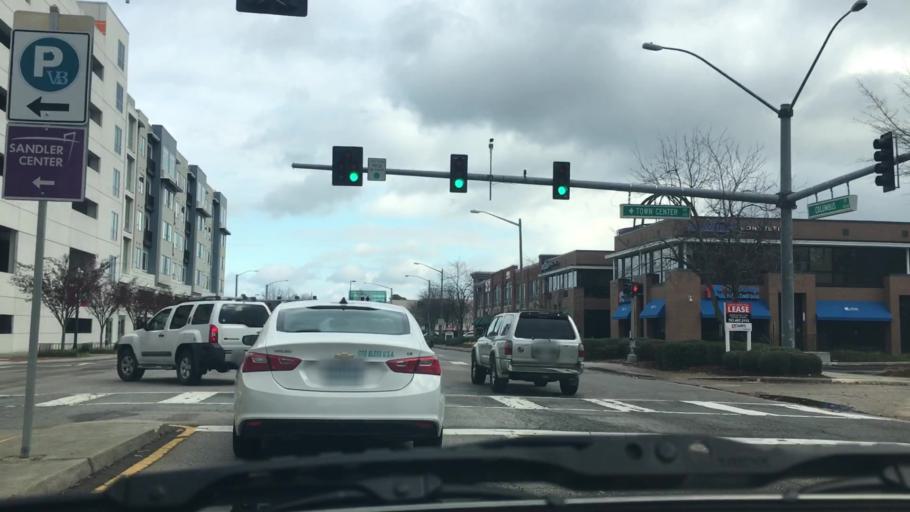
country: US
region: Virginia
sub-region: City of Chesapeake
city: Chesapeake
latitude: 36.8410
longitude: -76.1330
